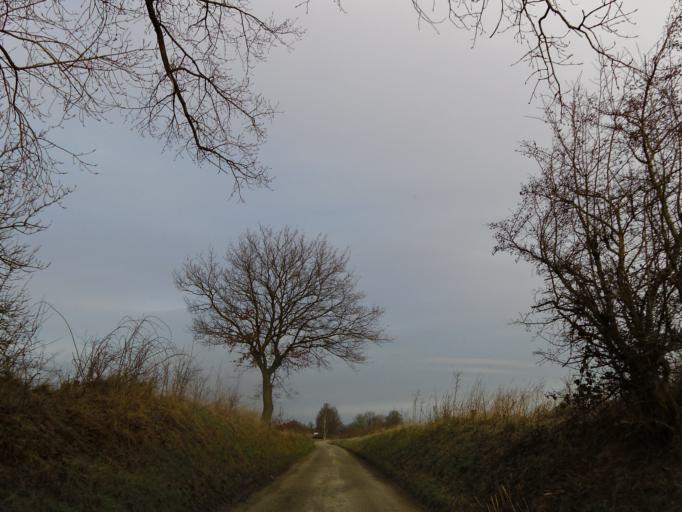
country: NL
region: Limburg
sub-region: Gemeente Voerendaal
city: Ubachsberg
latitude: 50.8370
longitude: 5.9553
